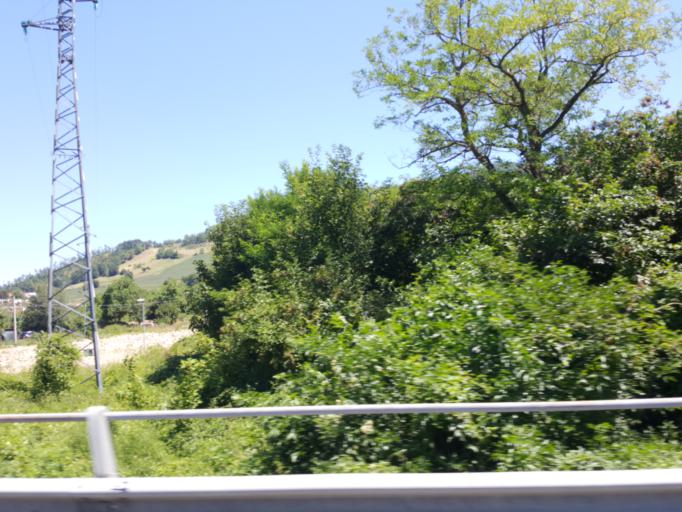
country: IT
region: Latium
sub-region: Provincia di Rieti
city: Accumoli
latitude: 42.7338
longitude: 13.2672
